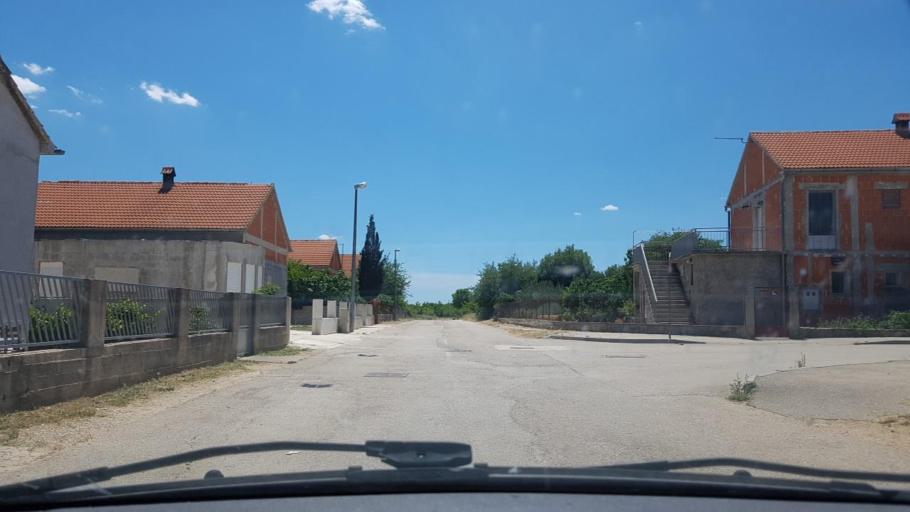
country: HR
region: Sibensko-Kniniska
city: Kistanje
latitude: 43.9804
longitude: 15.9732
